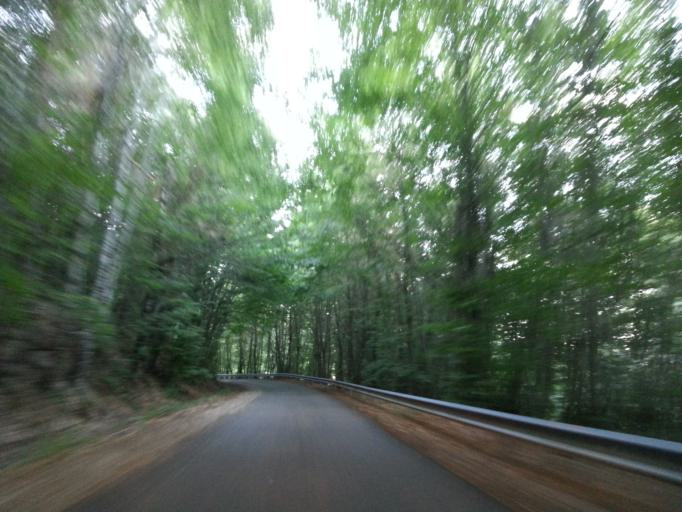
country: FR
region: Alsace
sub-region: Departement du Bas-Rhin
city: Lembach
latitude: 48.9850
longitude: 7.8407
